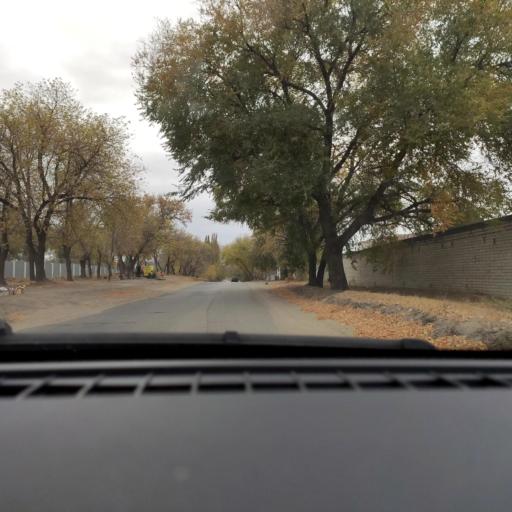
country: RU
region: Voronezj
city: Voronezh
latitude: 51.6618
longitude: 39.2897
